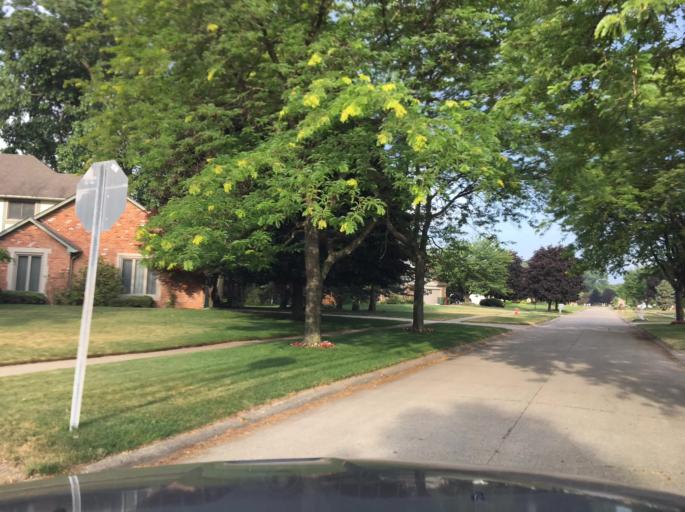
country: US
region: Michigan
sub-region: Macomb County
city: Utica
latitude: 42.6365
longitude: -83.0082
